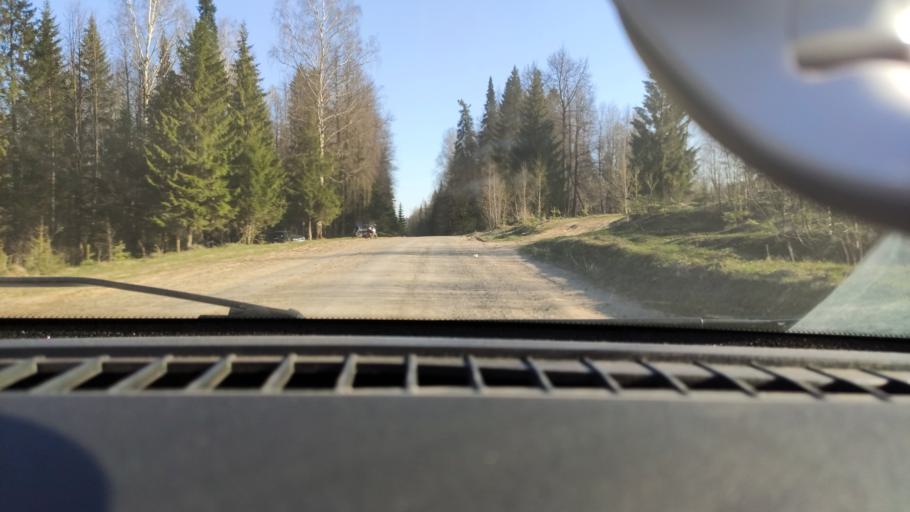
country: RU
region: Perm
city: Polazna
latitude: 58.1332
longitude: 56.4577
